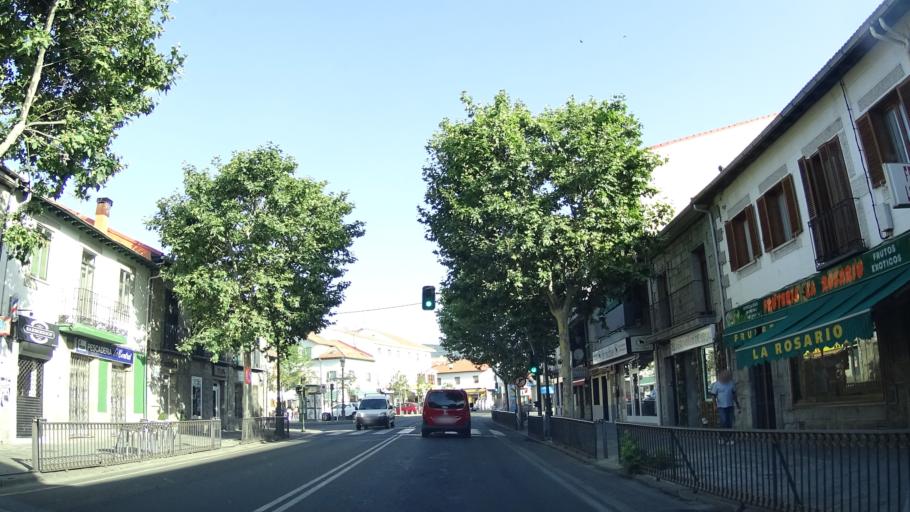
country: ES
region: Madrid
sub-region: Provincia de Madrid
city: Guadarrama
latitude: 40.6727
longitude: -4.0902
